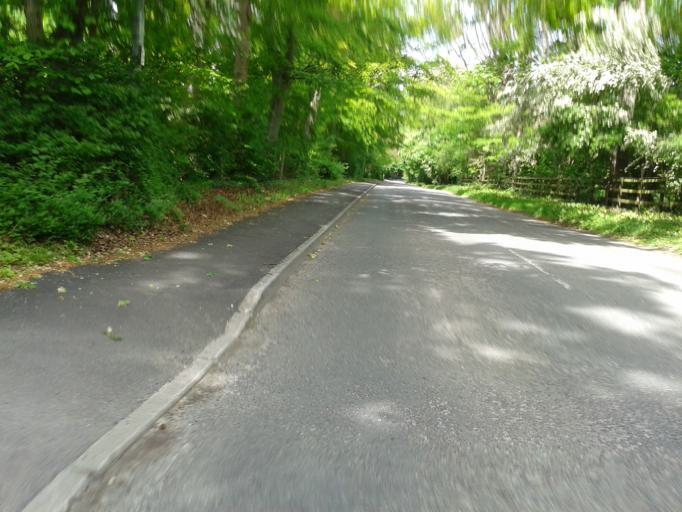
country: GB
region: England
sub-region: Cambridgeshire
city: Meldreth
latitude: 52.1088
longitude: 0.0408
